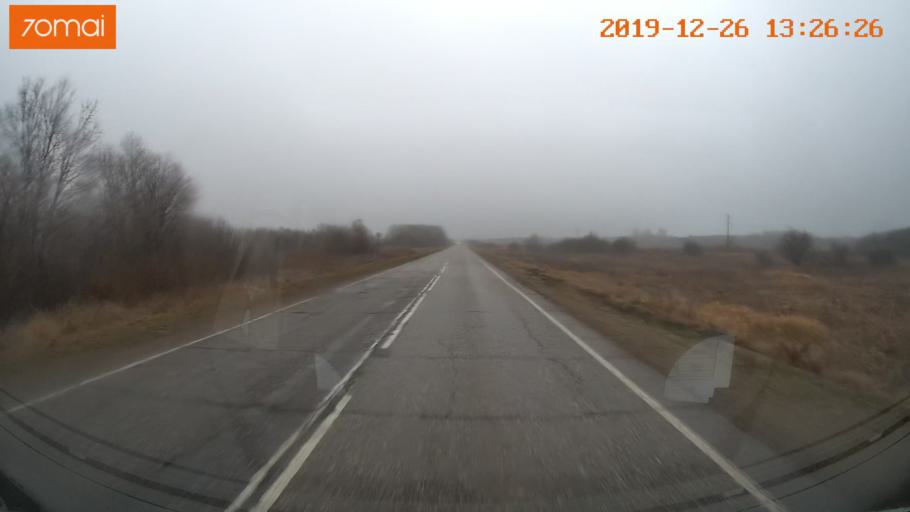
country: RU
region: Vologda
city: Cherepovets
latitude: 58.8642
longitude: 38.2256
